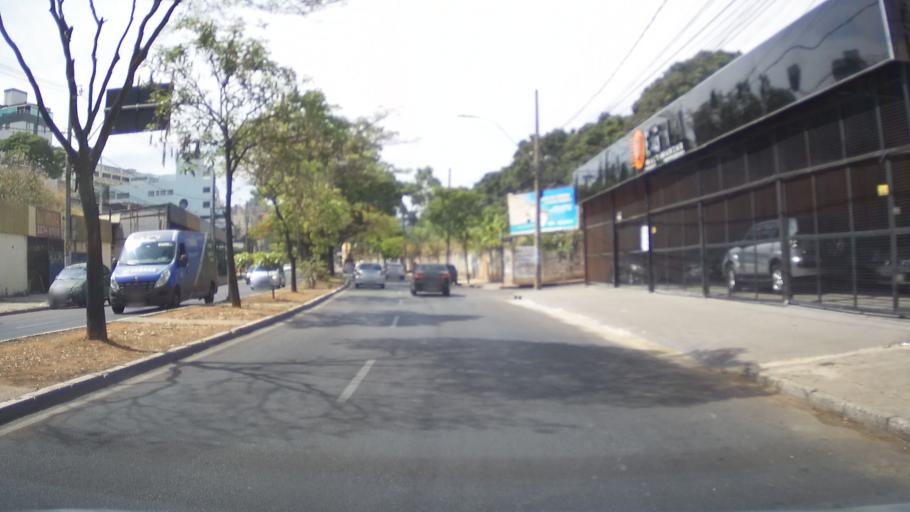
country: BR
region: Minas Gerais
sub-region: Belo Horizonte
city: Belo Horizonte
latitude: -19.9396
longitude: -43.9726
